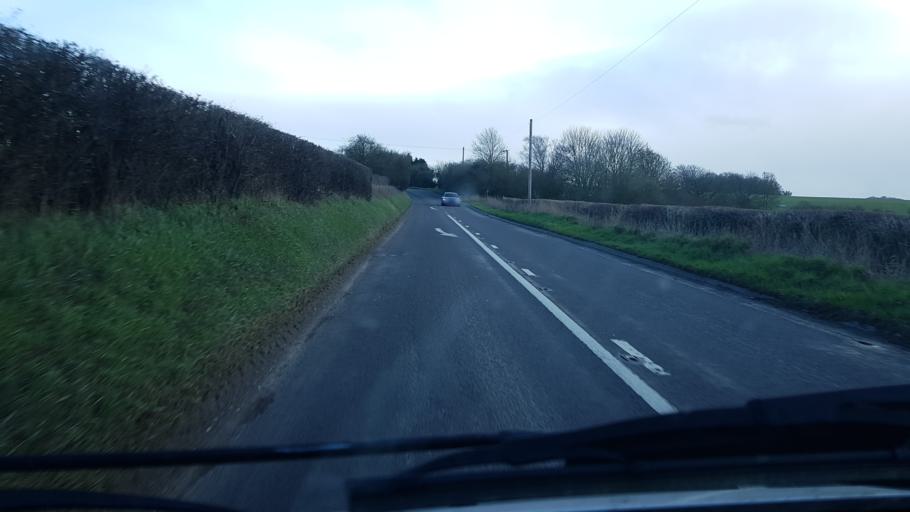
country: GB
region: England
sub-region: Wiltshire
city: Collingbourne Kingston
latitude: 51.2752
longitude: -1.6500
